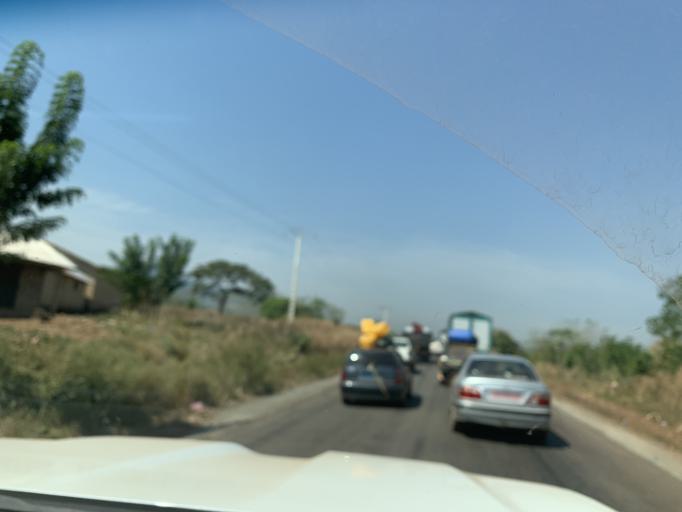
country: GN
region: Mamou
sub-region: Mamou Prefecture
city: Mamou
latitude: 10.1906
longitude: -12.4582
